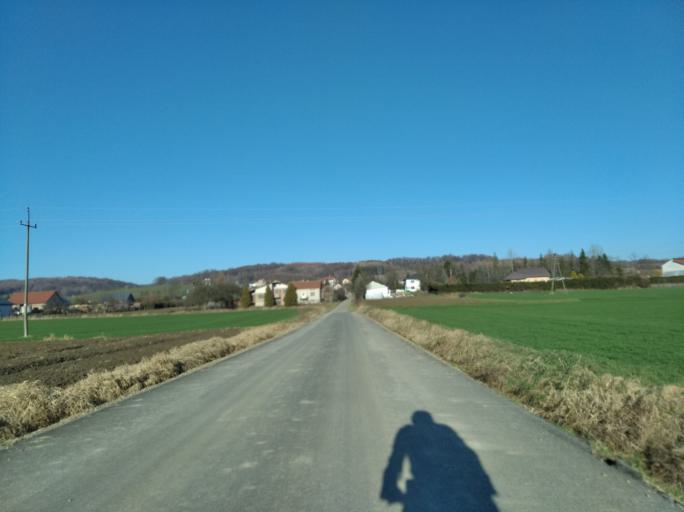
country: PL
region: Subcarpathian Voivodeship
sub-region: Powiat strzyzowski
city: Wisniowa
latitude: 49.8717
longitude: 21.6953
